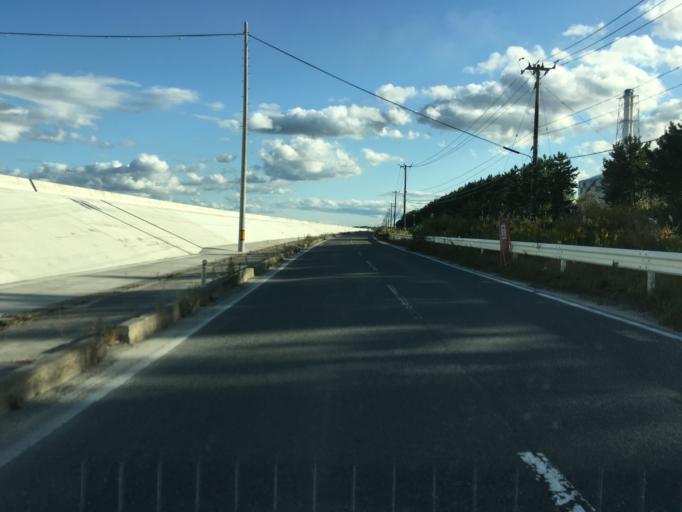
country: JP
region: Miyagi
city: Marumori
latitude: 37.8495
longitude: 140.9472
